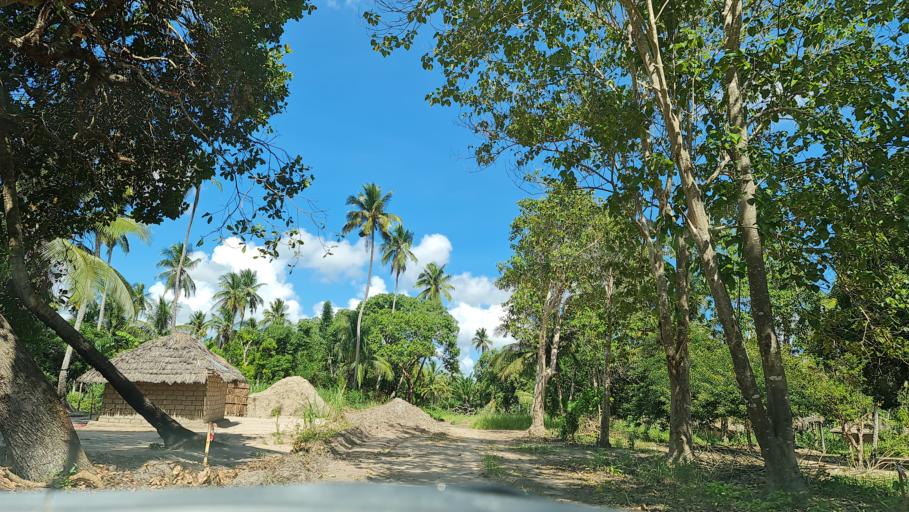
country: MZ
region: Zambezia
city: Quelimane
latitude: -17.3845
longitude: 37.5256
